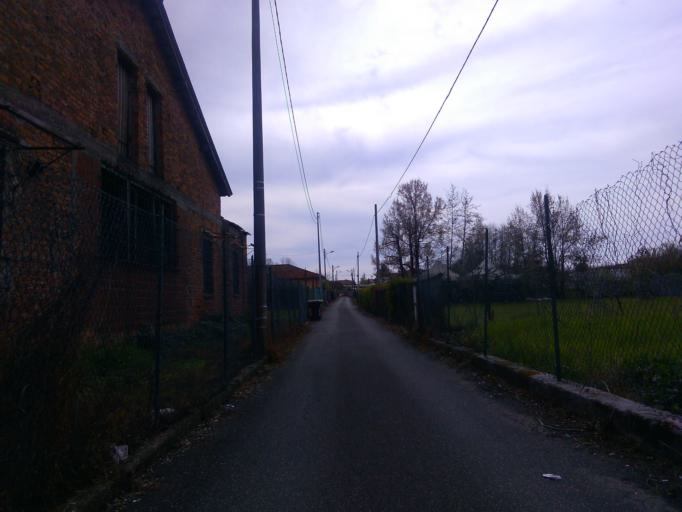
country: IT
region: Tuscany
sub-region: Provincia di Massa-Carrara
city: Marina di Carrara
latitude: 44.0519
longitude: 10.0412
